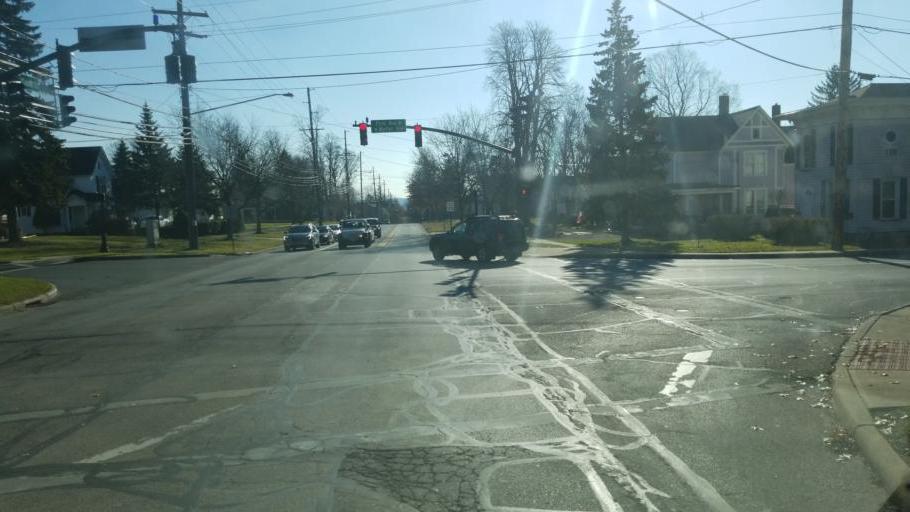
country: US
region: Ohio
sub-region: Geauga County
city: Chardon
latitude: 41.5779
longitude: -81.2035
